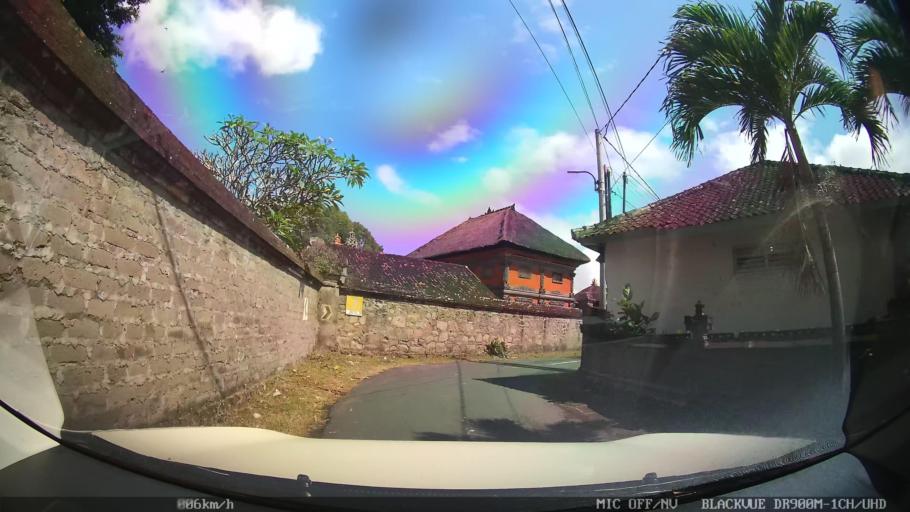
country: ID
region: Bali
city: Banjar Sedang
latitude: -8.5571
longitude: 115.2694
